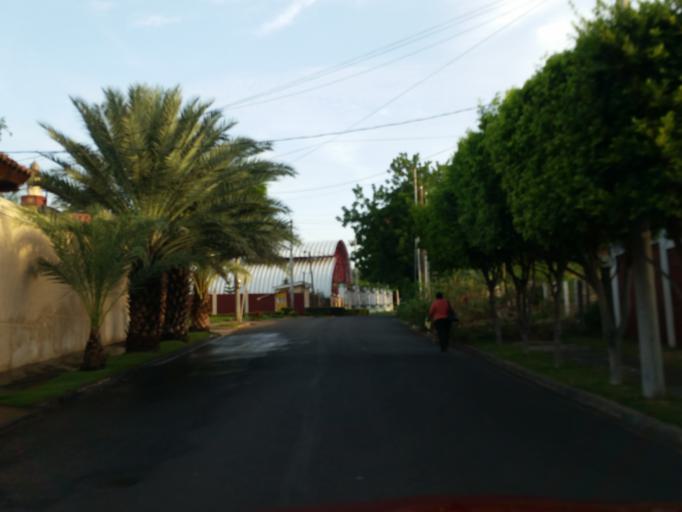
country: NI
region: Managua
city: Managua
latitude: 12.1142
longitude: -86.2696
